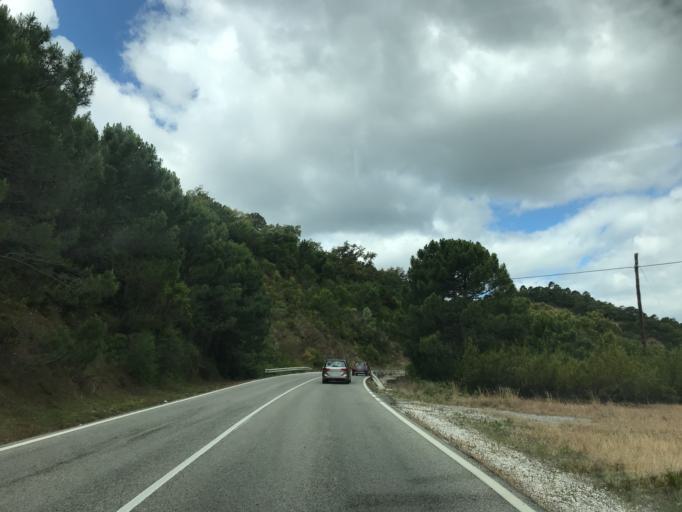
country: ES
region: Andalusia
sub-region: Provincia de Malaga
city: Benahavis
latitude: 36.5417
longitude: -5.0143
